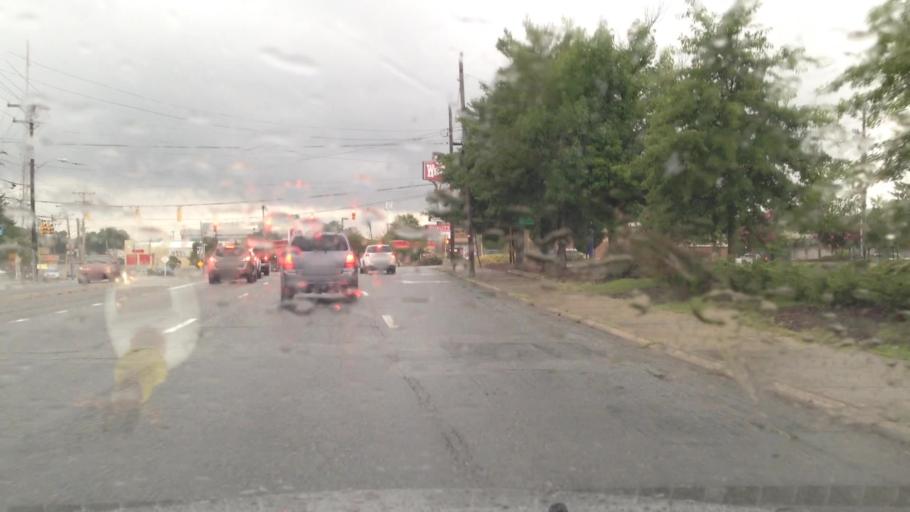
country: US
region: North Carolina
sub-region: Guilford County
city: Greensboro
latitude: 36.0625
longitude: -79.8145
